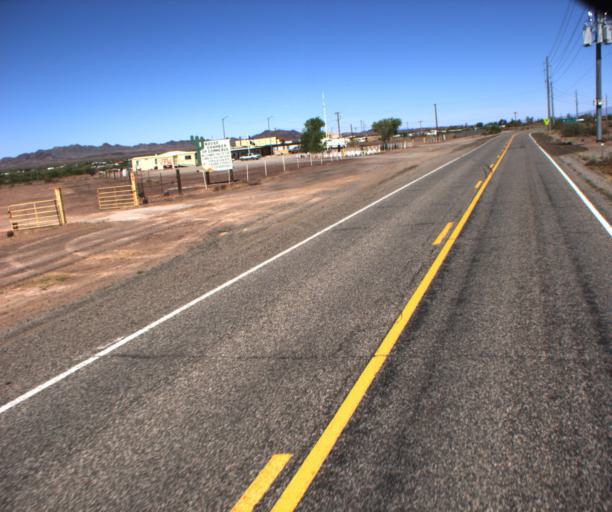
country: US
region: Arizona
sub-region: La Paz County
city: Quartzsite
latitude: 33.9116
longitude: -113.9885
